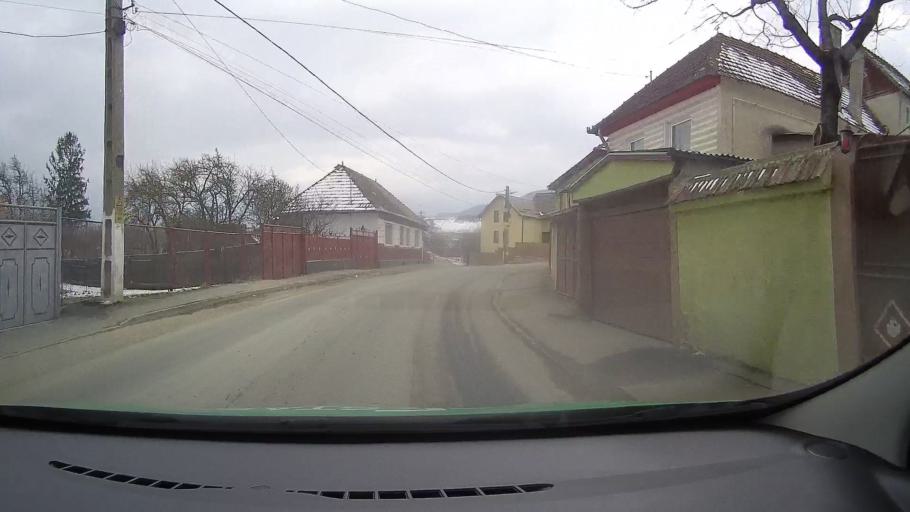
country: RO
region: Brasov
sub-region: Comuna Zarnesti
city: Zarnesti
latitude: 45.5567
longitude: 25.3254
